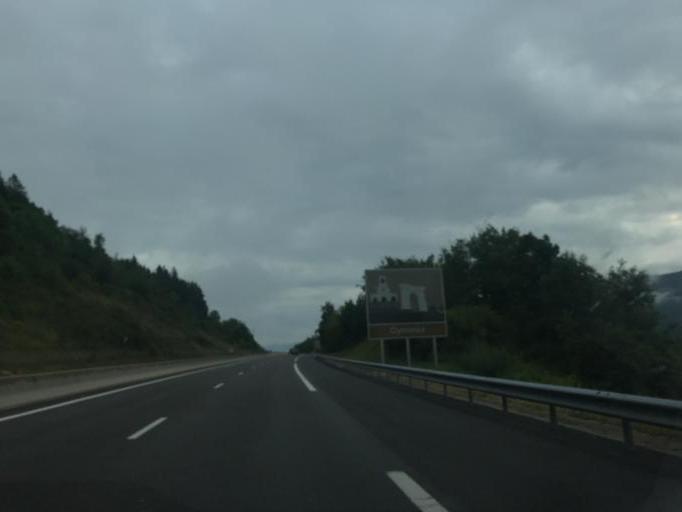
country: FR
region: Rhone-Alpes
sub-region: Departement de l'Ain
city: Martignat
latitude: 46.2039
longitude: 5.5946
